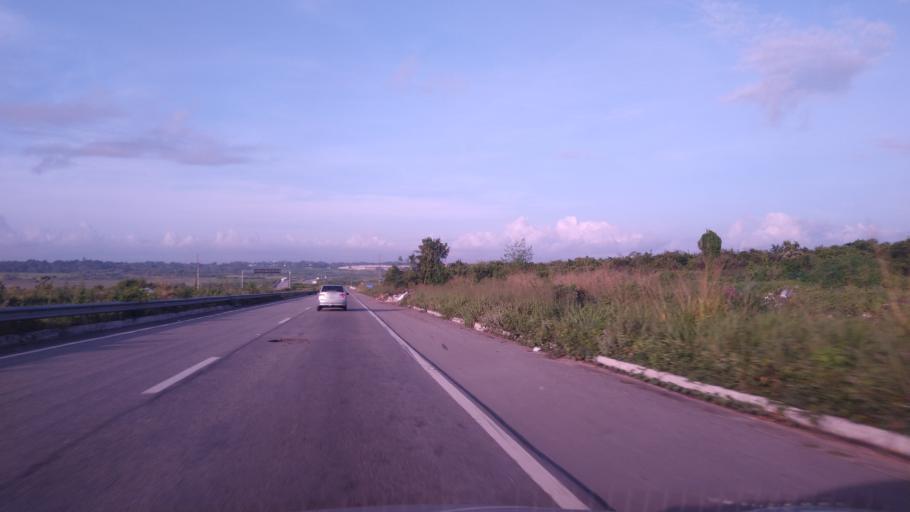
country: BR
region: Ceara
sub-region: Pacajus
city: Pacajus
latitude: -4.1531
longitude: -38.4804
